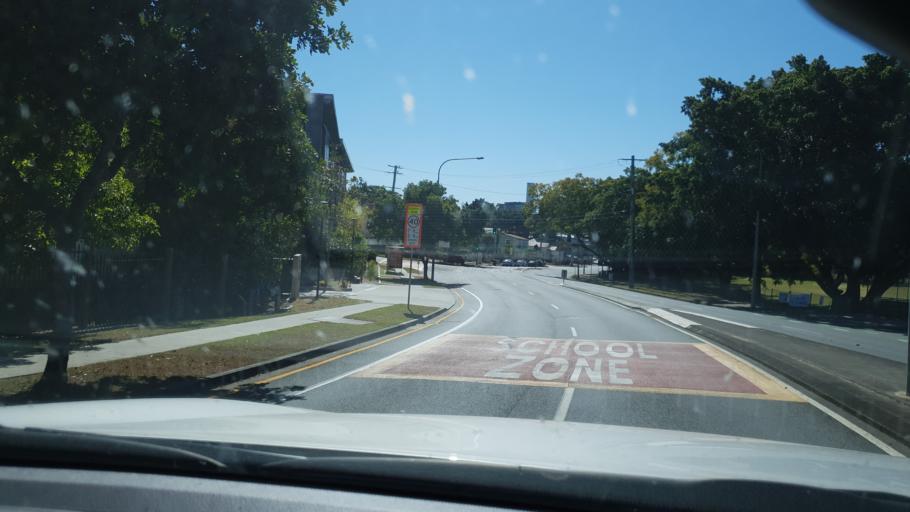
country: AU
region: Queensland
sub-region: Brisbane
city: Woolloongabba
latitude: -27.4944
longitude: 153.0278
